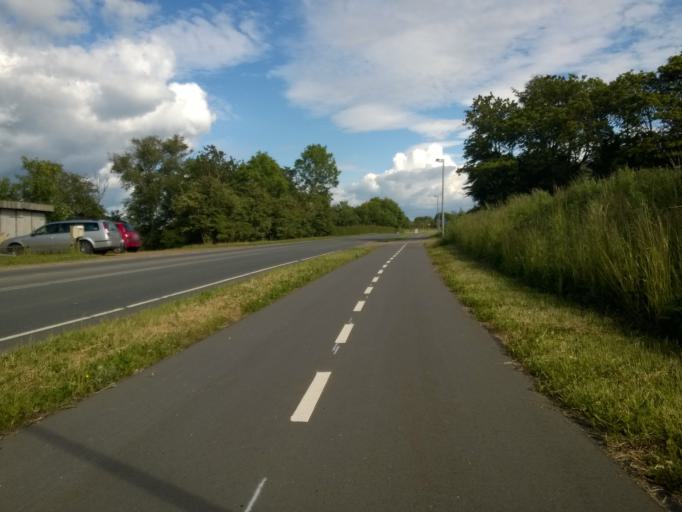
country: DK
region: Central Jutland
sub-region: Holstebro Kommune
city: Vinderup
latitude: 56.4594
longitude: 8.8606
